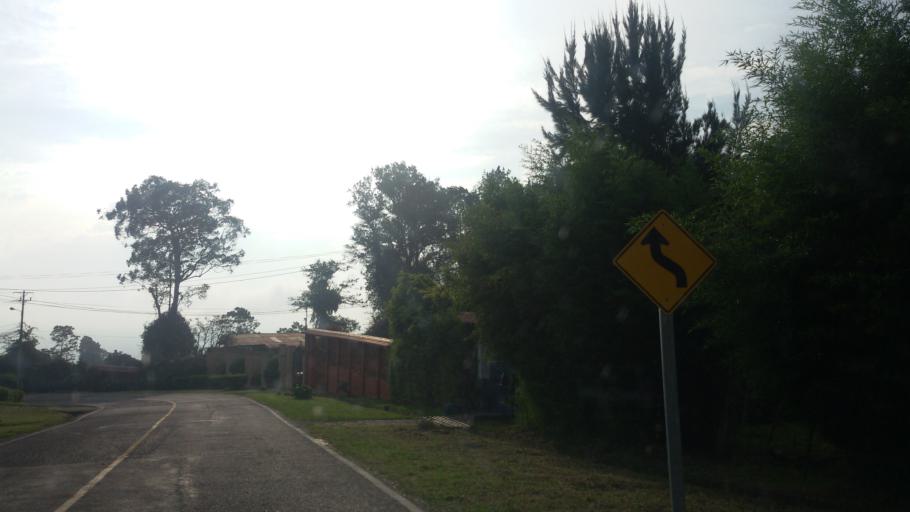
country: CR
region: San Jose
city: Ipis
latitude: 9.9846
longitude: -83.9629
